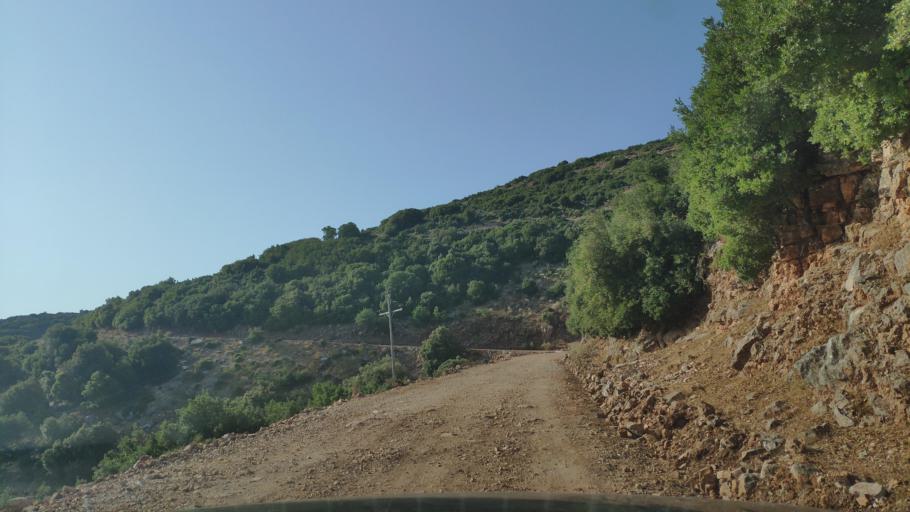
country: GR
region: West Greece
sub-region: Nomos Aitolias kai Akarnanias
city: Monastirakion
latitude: 38.8379
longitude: 20.9787
